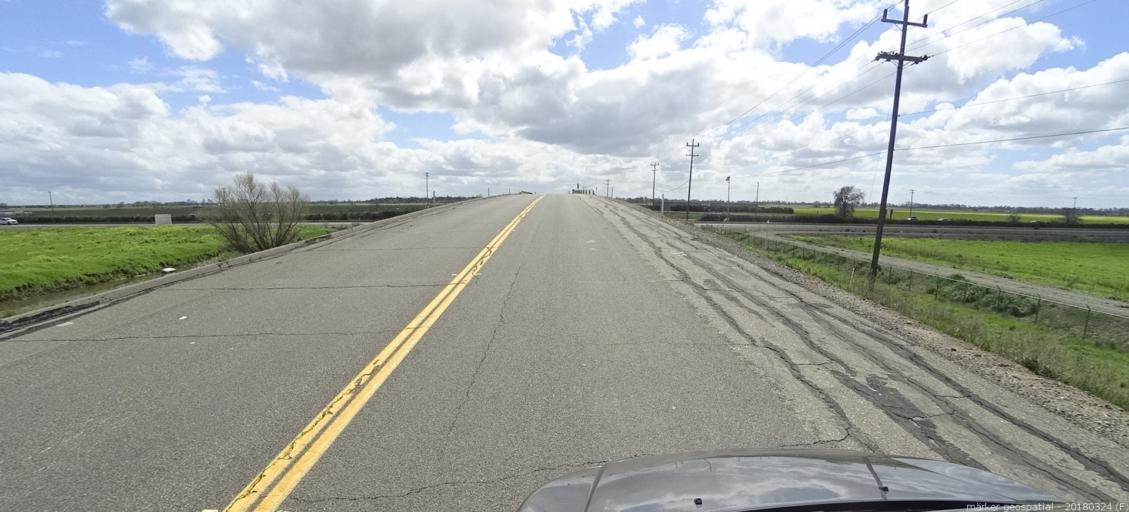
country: US
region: California
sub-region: Yolo County
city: West Sacramento
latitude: 38.6724
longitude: -121.5764
